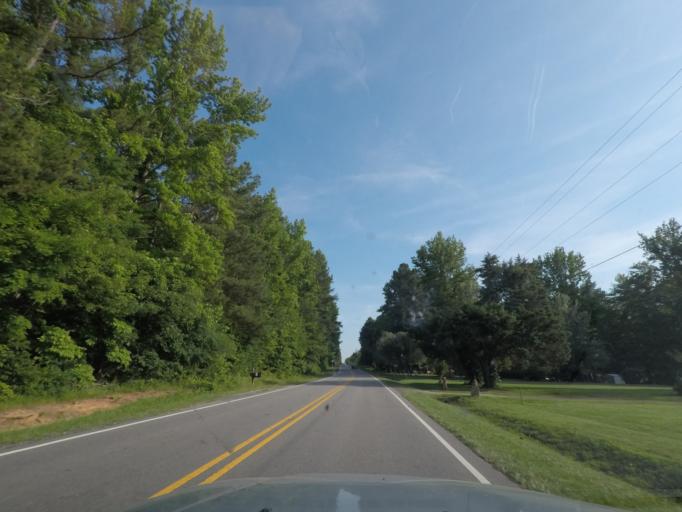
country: US
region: North Carolina
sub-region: Granville County
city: Oxford
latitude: 36.3970
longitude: -78.5924
